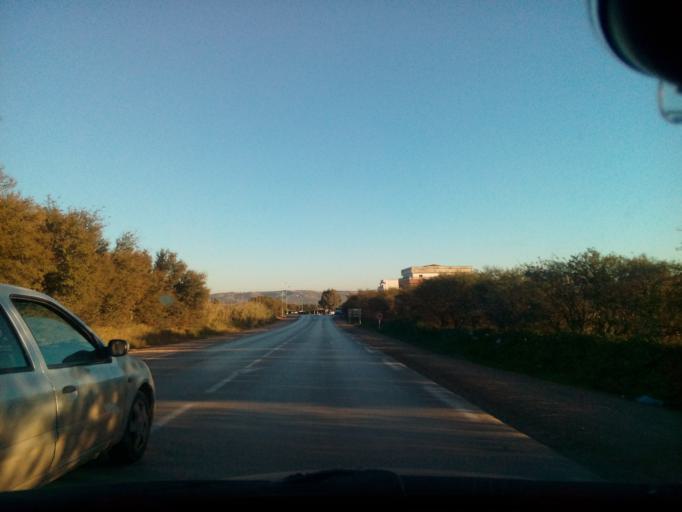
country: DZ
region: Mostaganem
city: Mostaganem
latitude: 35.7596
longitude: 0.2190
